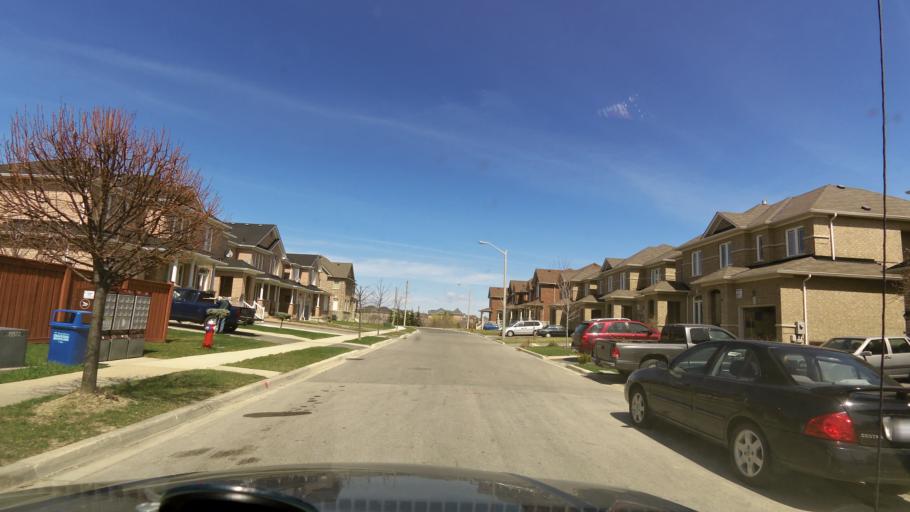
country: CA
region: Ontario
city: Brampton
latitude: 43.7137
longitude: -79.8241
